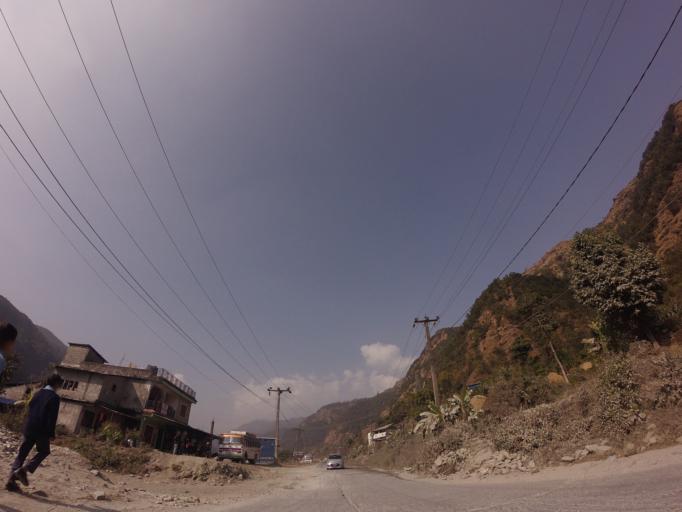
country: NP
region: Western Region
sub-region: Gandaki Zone
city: Pokhara
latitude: 28.2873
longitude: 83.8987
